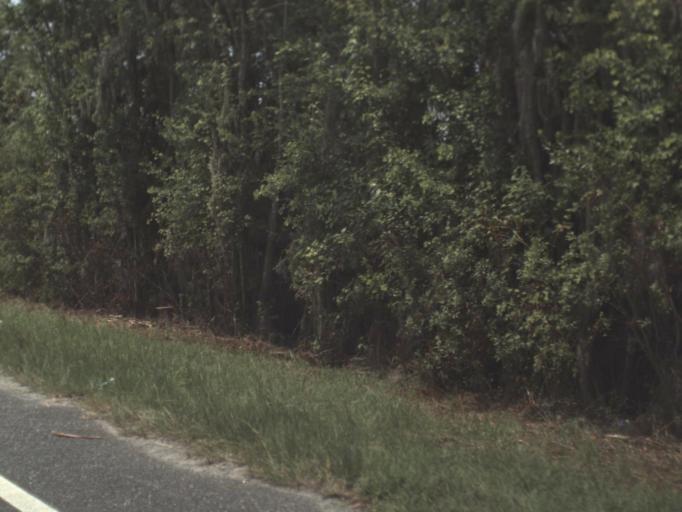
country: US
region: Georgia
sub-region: Echols County
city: Statenville
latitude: 30.6114
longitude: -83.1085
